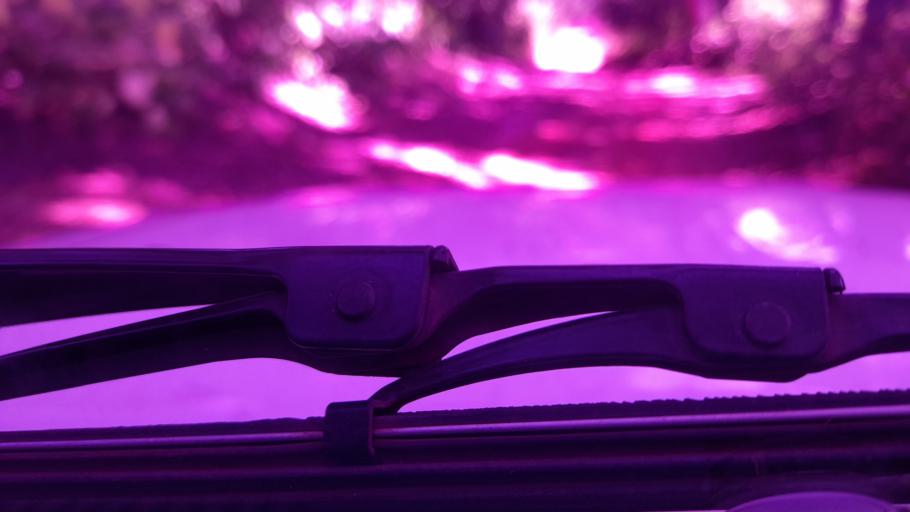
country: GW
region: Oio
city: Bissora
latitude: 12.3976
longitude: -15.6689
